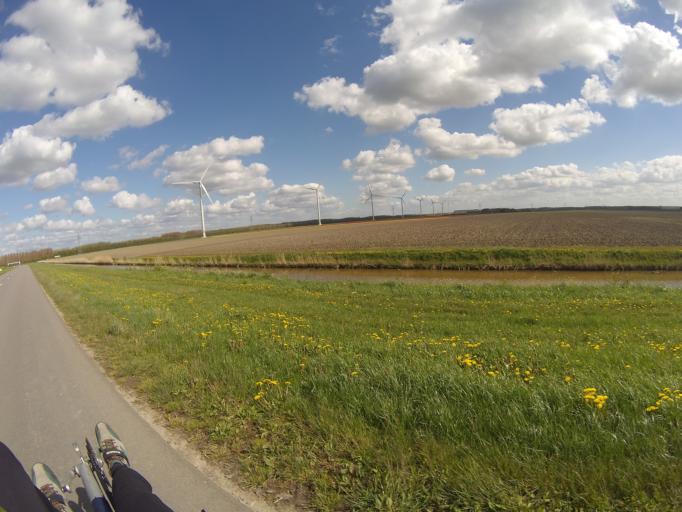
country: NL
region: Utrecht
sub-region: Gemeente Bunschoten
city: Bunschoten
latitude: 52.3086
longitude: 5.4331
